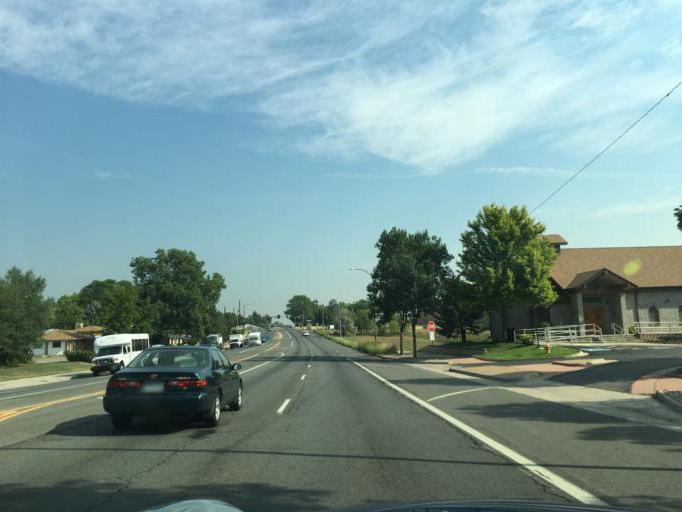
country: US
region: Colorado
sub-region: Jefferson County
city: Wheat Ridge
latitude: 39.7522
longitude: -105.0813
